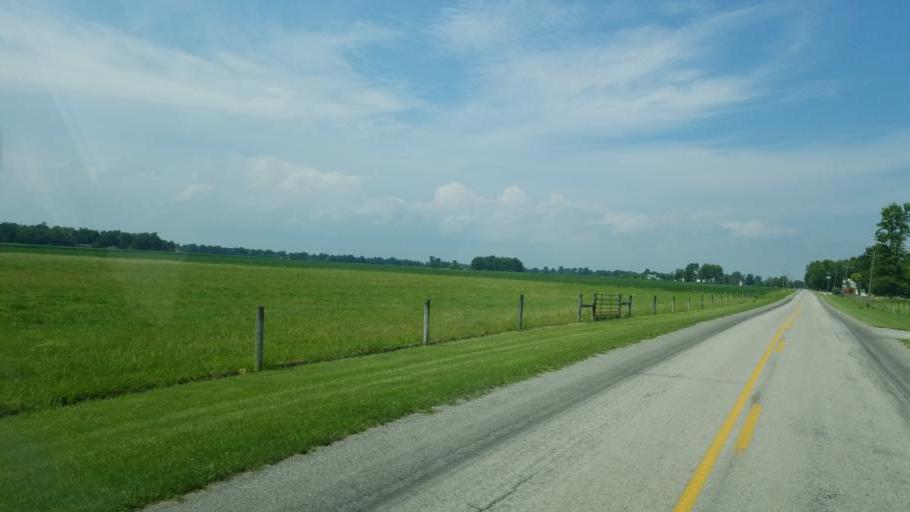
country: US
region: Ohio
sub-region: Union County
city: Richwood
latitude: 40.3692
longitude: -83.3483
